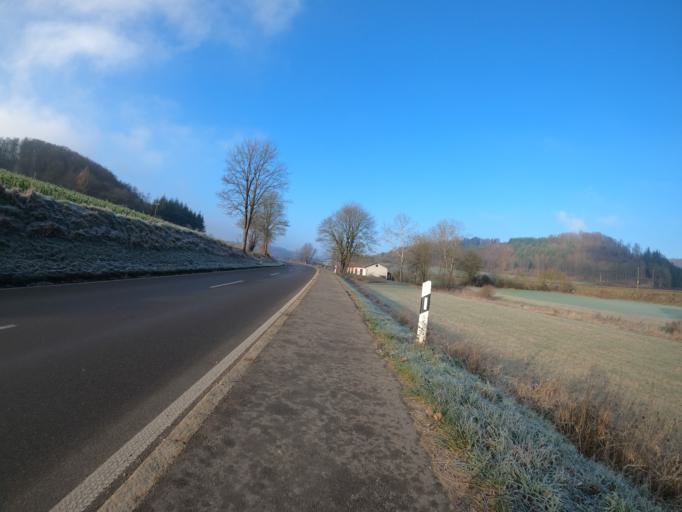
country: DE
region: Baden-Wuerttemberg
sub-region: Tuebingen Region
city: Lonsee
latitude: 48.5474
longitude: 9.9115
